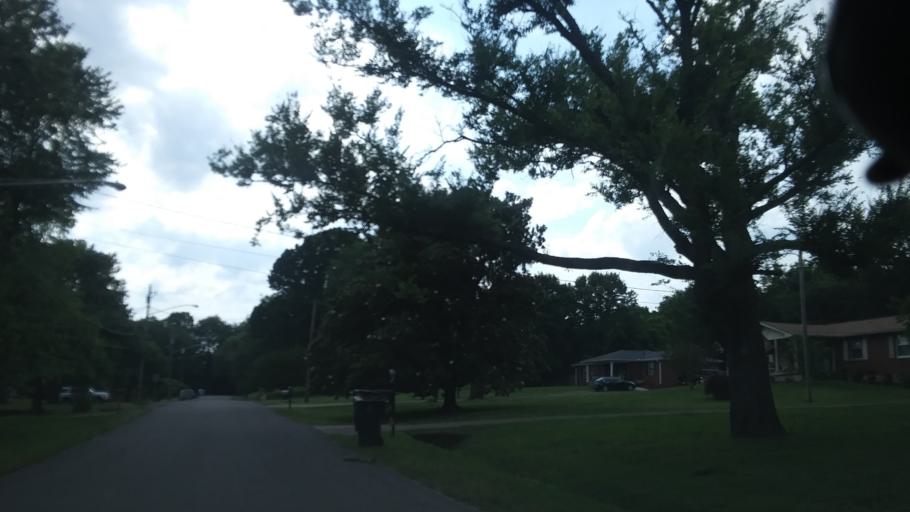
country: US
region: Tennessee
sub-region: Rutherford County
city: La Vergne
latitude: 36.0902
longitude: -86.6629
